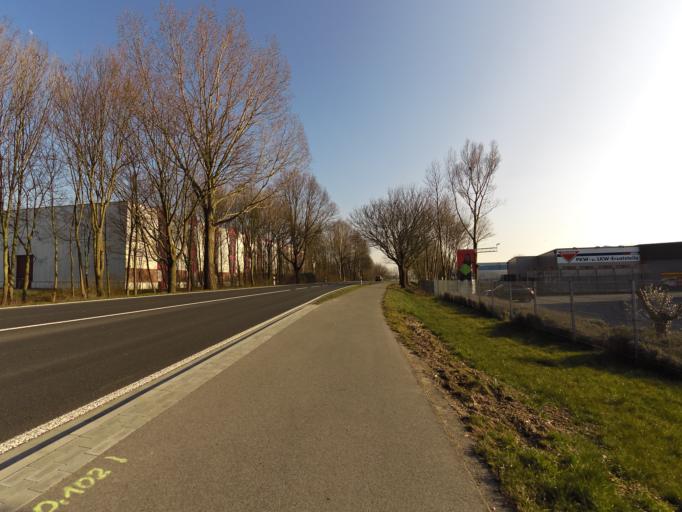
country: DE
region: North Rhine-Westphalia
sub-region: Regierungsbezirk Dusseldorf
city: Emmerich
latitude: 51.8408
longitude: 6.2751
